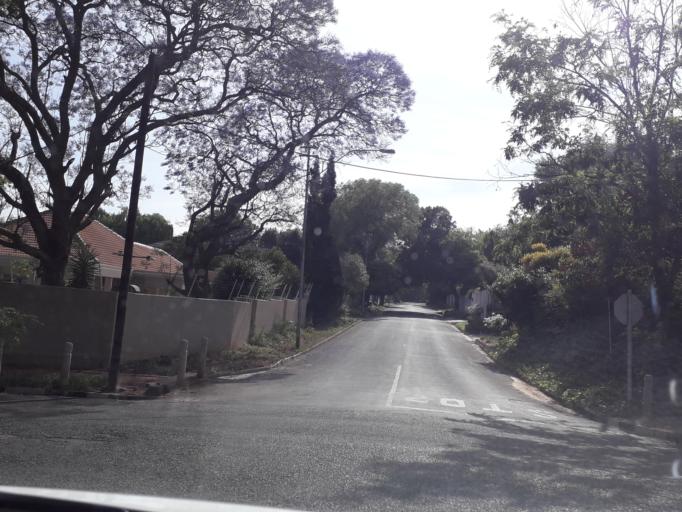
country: ZA
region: Gauteng
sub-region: City of Johannesburg Metropolitan Municipality
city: Johannesburg
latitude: -26.1728
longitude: 28.0353
